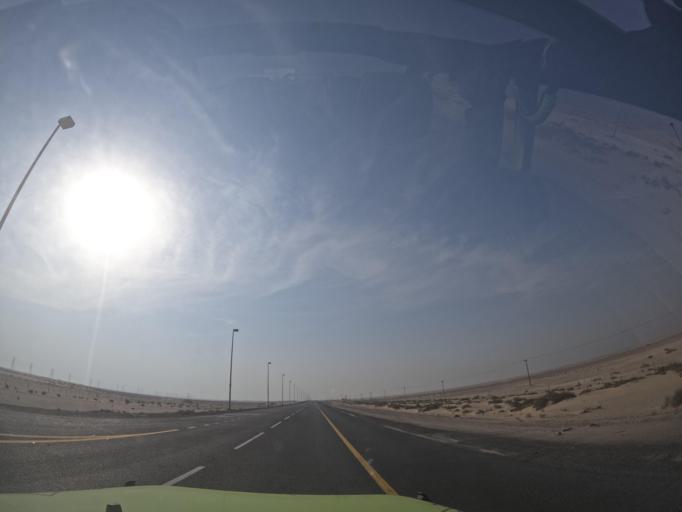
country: AE
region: Dubai
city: Dubai
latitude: 24.7645
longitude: 55.0955
